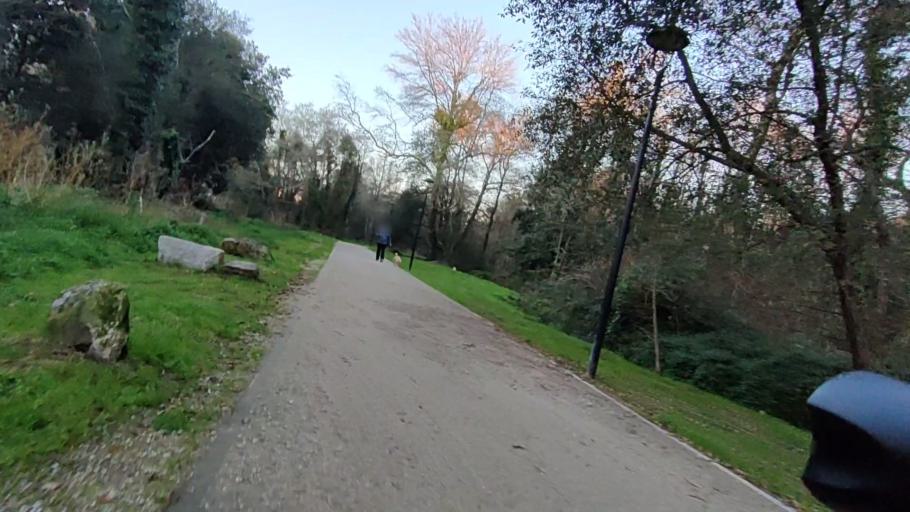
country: ES
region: Galicia
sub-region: Provincia da Coruna
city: Boiro
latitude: 42.6408
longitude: -8.8796
